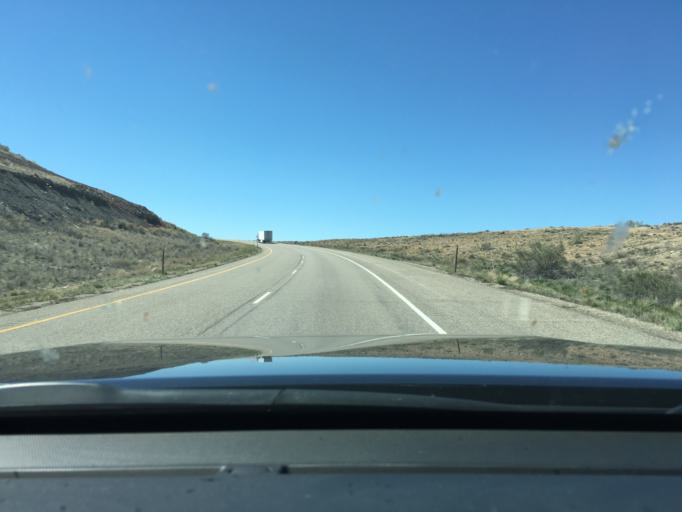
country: US
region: Colorado
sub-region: Mesa County
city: Loma
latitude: 39.2328
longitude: -108.9064
